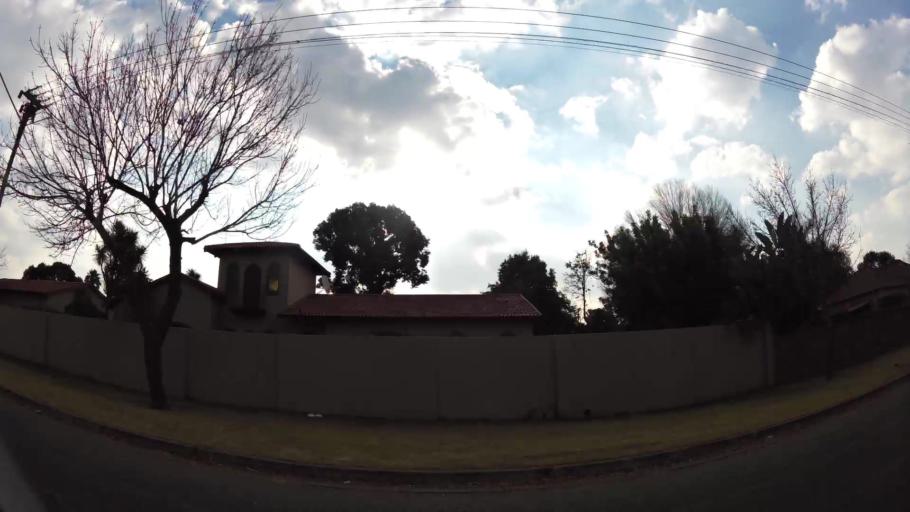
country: ZA
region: Gauteng
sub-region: Ekurhuleni Metropolitan Municipality
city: Germiston
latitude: -26.2507
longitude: 28.1773
